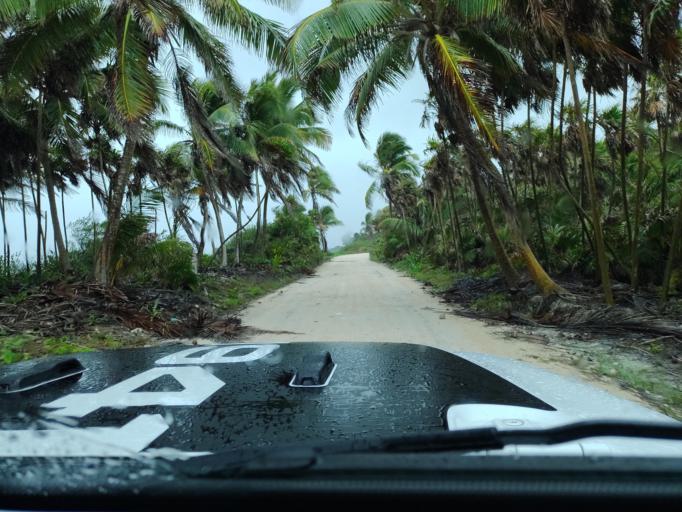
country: MX
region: Quintana Roo
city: Tulum
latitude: 19.9797
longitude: -87.4684
